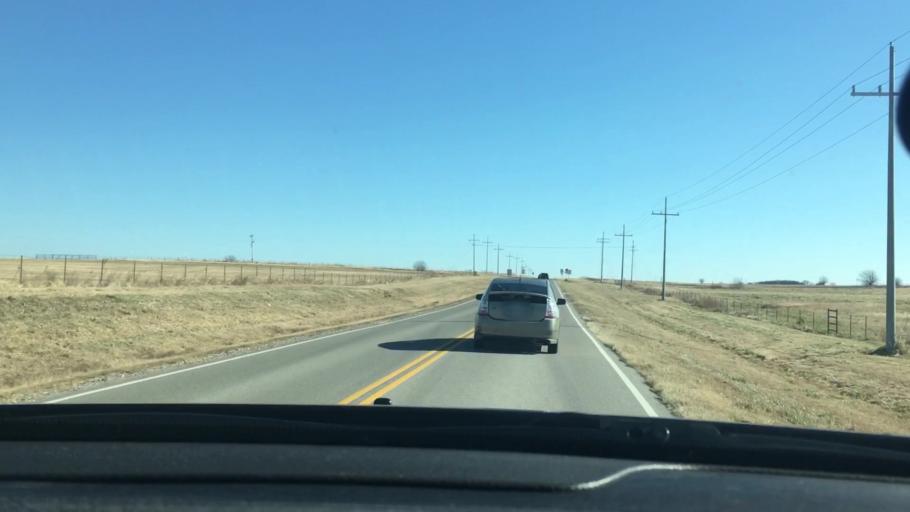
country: US
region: Oklahoma
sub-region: Murray County
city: Davis
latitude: 34.4773
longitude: -97.0935
